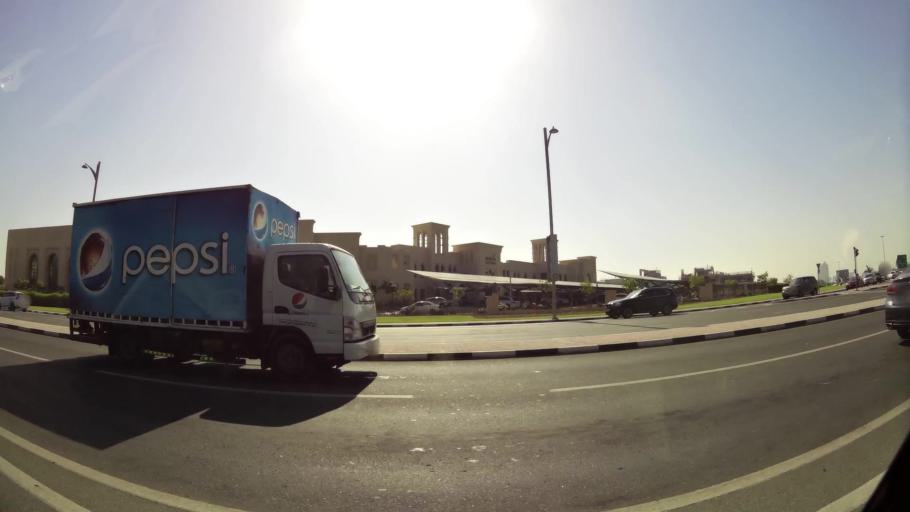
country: AE
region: Dubai
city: Dubai
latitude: 25.1332
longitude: 55.1882
